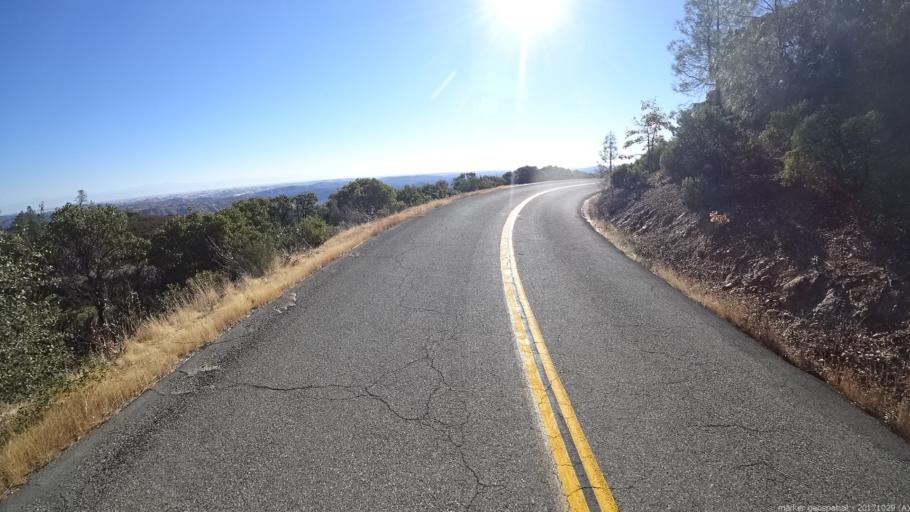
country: US
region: California
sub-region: Trinity County
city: Lewiston
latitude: 40.3671
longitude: -122.8474
